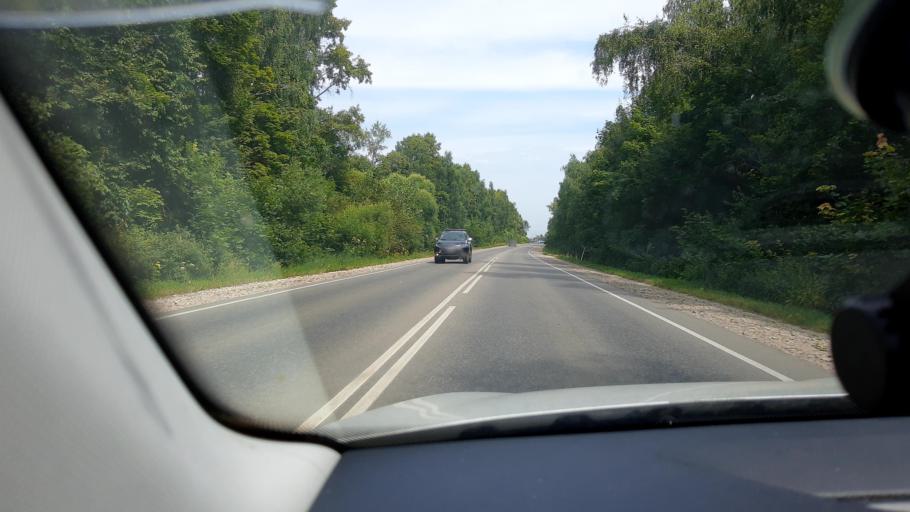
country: RU
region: Tula
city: Zaokskiy
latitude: 54.7439
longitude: 37.4297
